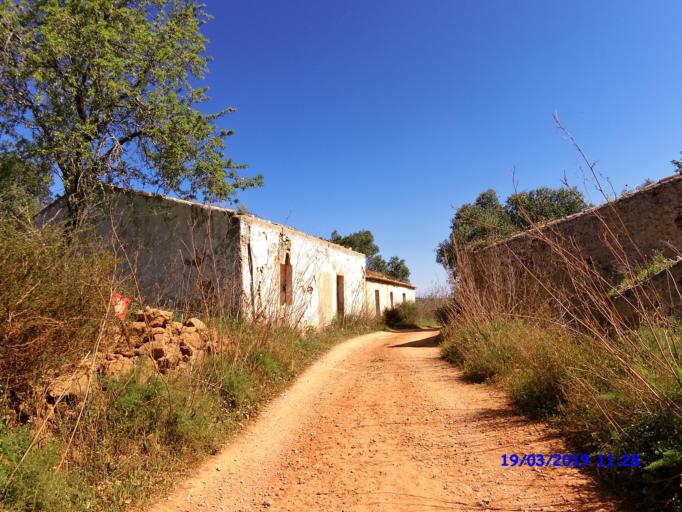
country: PT
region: Faro
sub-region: Loule
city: Boliqueime
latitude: 37.2118
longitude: -8.1481
